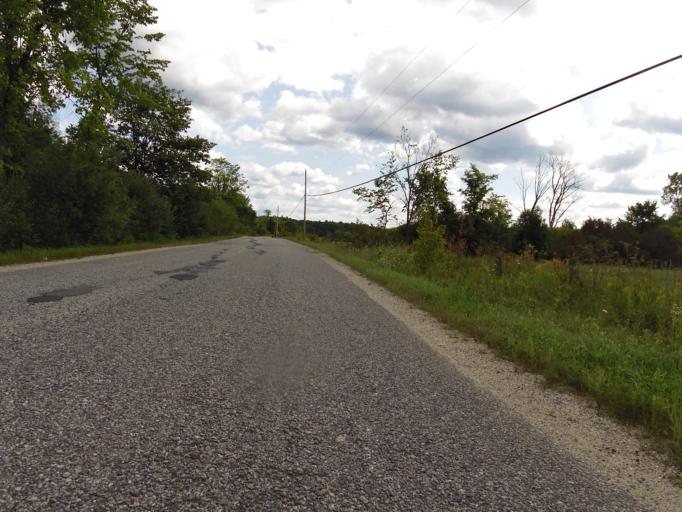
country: CA
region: Quebec
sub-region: Outaouais
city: Wakefield
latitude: 45.8096
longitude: -76.0155
